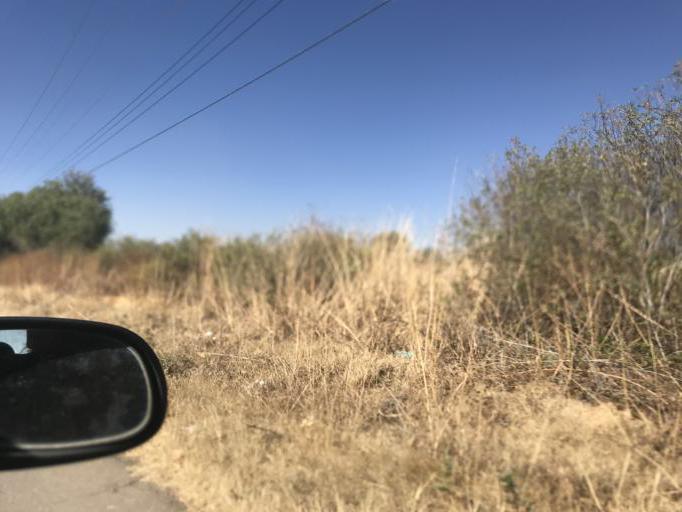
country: BO
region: Cochabamba
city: Tarata
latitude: -17.6057
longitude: -65.9947
